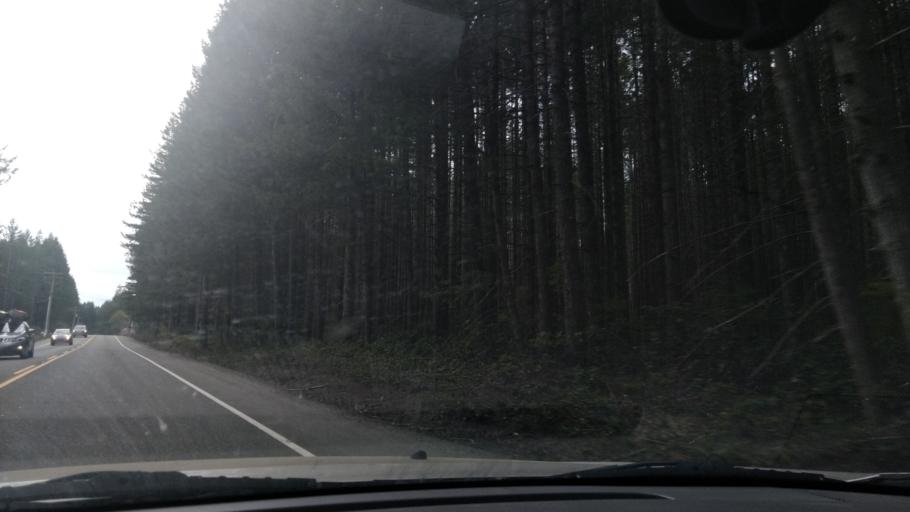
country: CA
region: British Columbia
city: Campbell River
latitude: 50.0313
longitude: -125.3413
